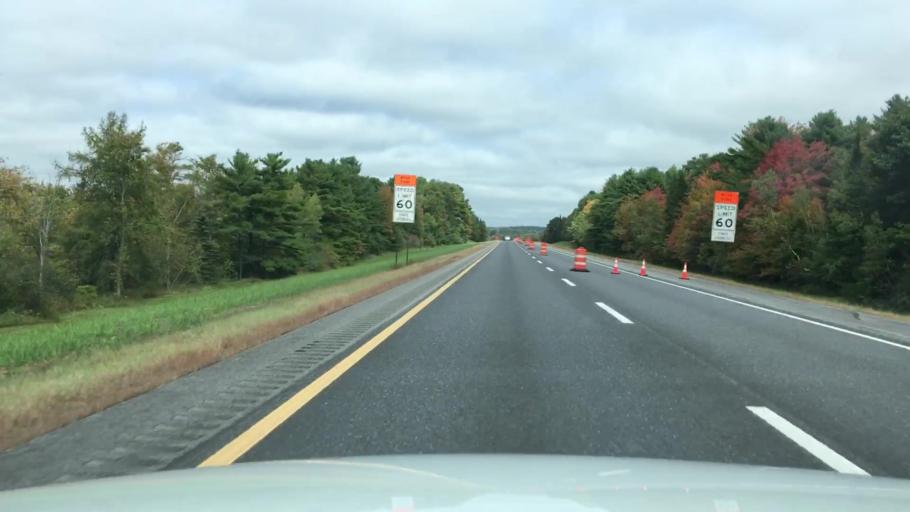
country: US
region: Maine
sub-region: Sagadahoc County
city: Richmond
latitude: 44.1383
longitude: -69.8433
